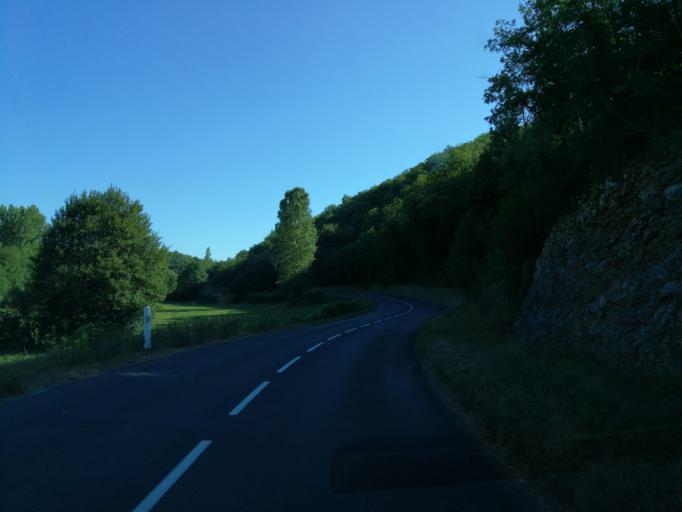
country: FR
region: Midi-Pyrenees
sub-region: Departement du Lot
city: Salviac
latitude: 44.7001
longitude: 1.2960
